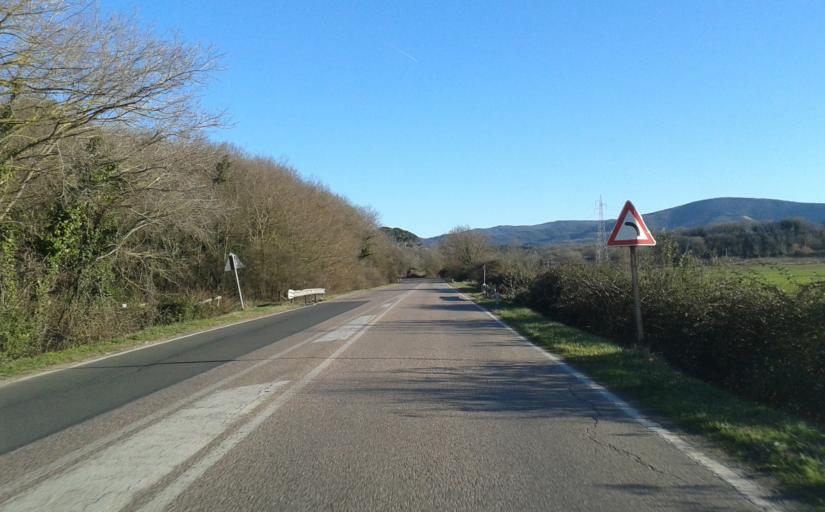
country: IT
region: Tuscany
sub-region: Provincia di Livorno
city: Livorno
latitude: 43.5700
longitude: 10.3560
